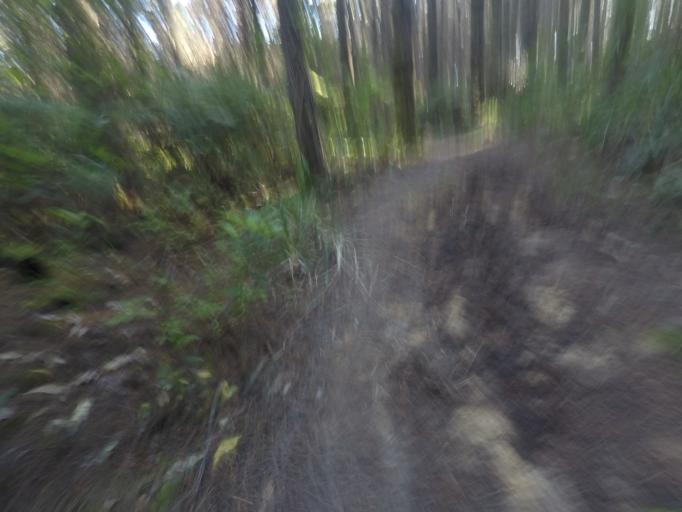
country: NZ
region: Auckland
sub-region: Auckland
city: Muriwai Beach
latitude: -36.7464
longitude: 174.5565
